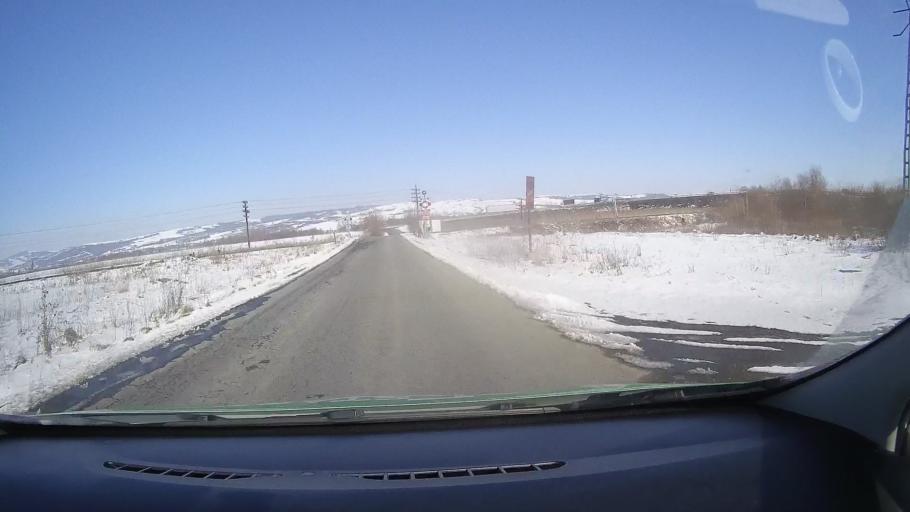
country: RO
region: Brasov
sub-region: Comuna Mandra
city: Mandra
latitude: 45.8304
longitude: 25.0134
